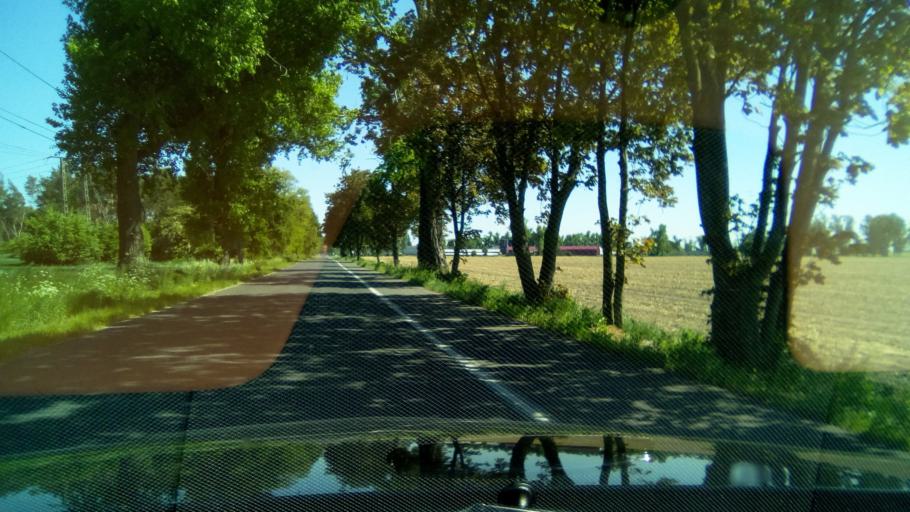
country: PL
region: Greater Poland Voivodeship
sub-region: Powiat gnieznienski
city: Gniezno
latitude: 52.4582
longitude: 17.5698
